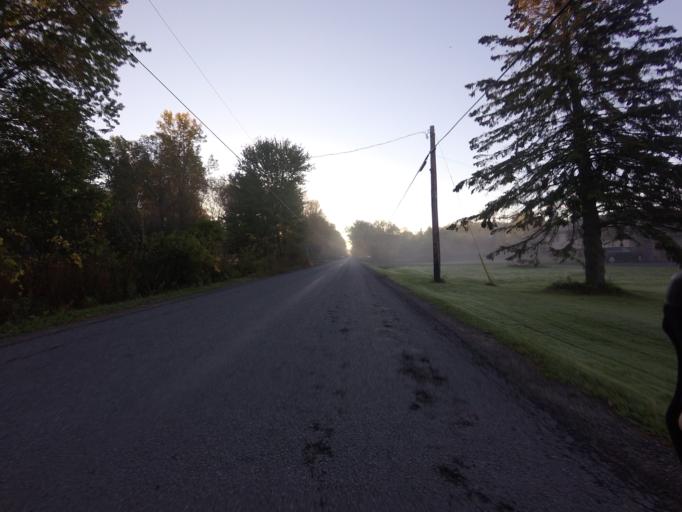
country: CA
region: Ontario
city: Quinte West
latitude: 44.0363
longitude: -77.5870
